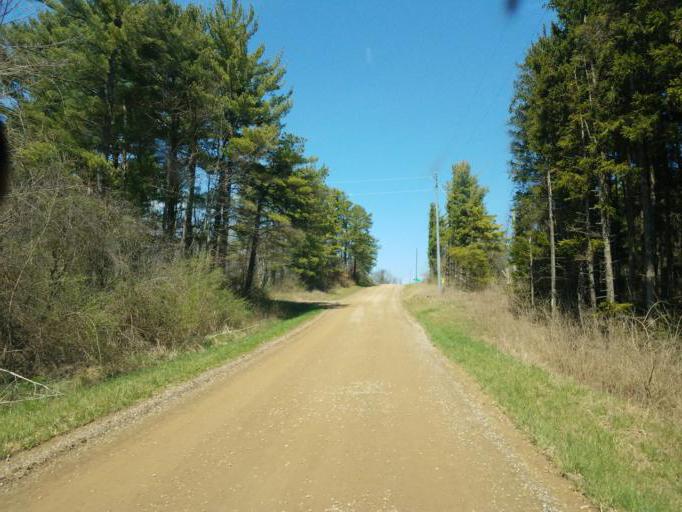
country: US
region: Ohio
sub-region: Knox County
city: Oak Hill
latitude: 40.3546
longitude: -82.1923
